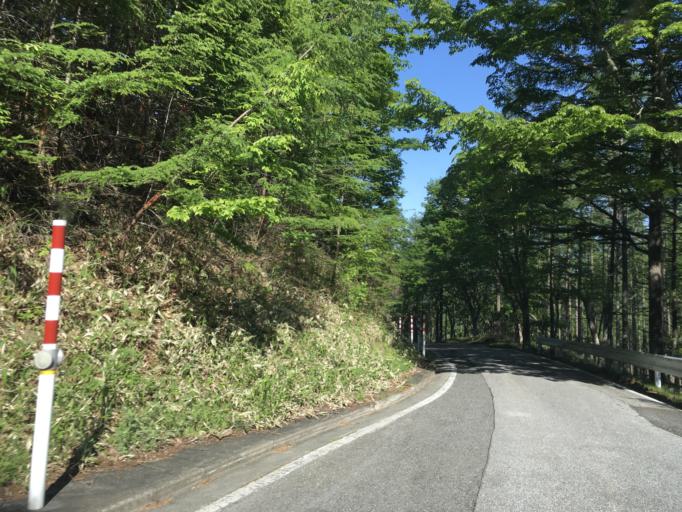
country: JP
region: Iwate
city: Ofunato
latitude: 39.1815
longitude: 141.7426
